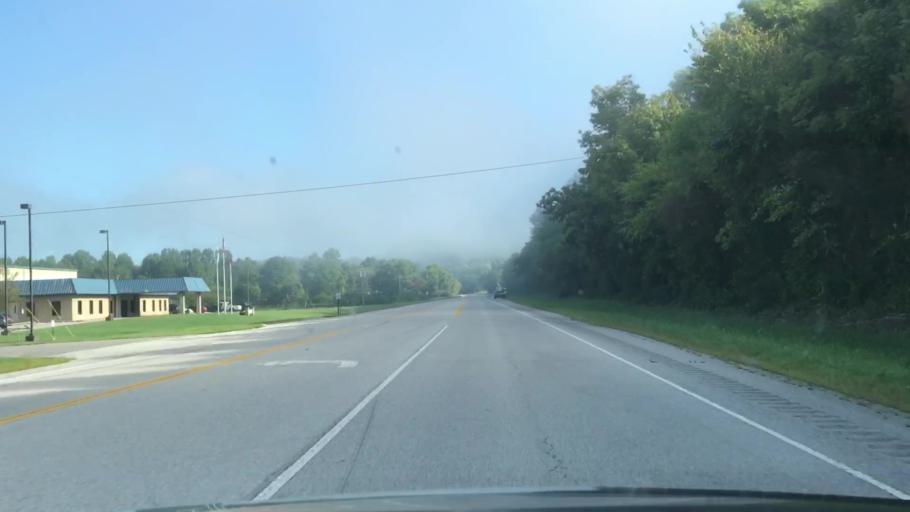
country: US
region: Tennessee
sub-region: Jackson County
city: Gainesboro
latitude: 36.3925
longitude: -85.6354
